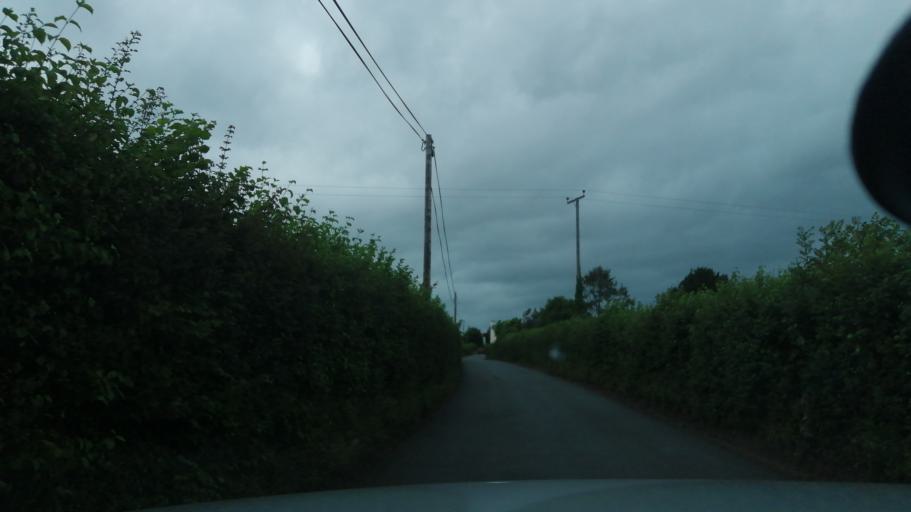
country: GB
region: England
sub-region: Herefordshire
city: Thruxton
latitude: 52.0082
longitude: -2.8069
